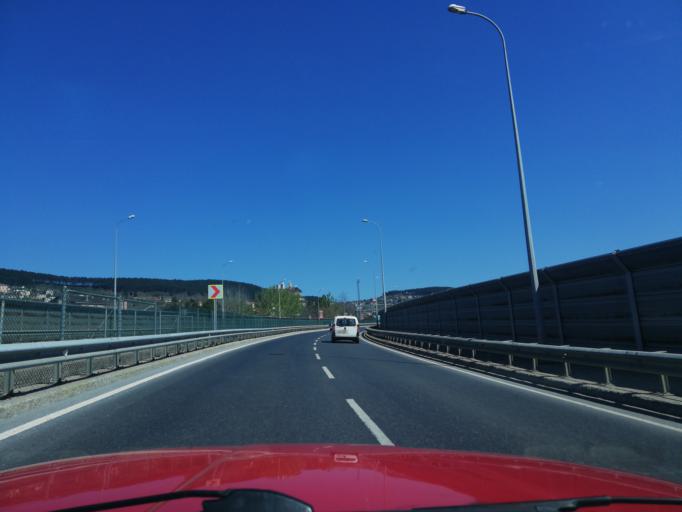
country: TR
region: Istanbul
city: Mahmut Sevket Pasa
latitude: 41.1169
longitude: 29.1205
